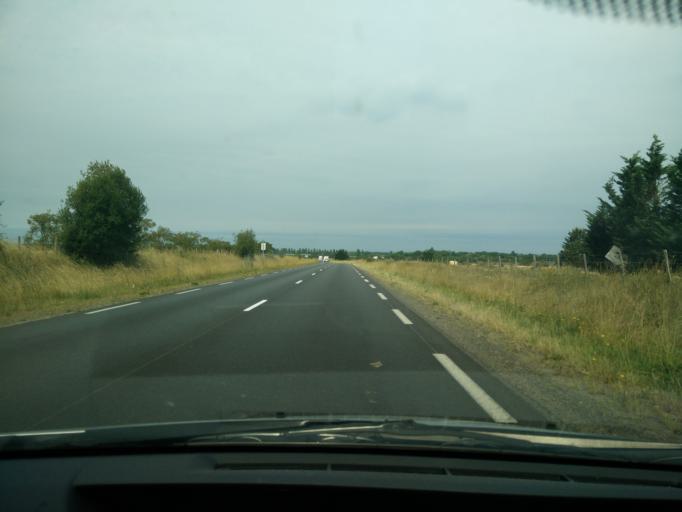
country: FR
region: Pays de la Loire
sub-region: Departement de Maine-et-Loire
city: Doue-la-Fontaine
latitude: 47.1834
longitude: -0.2902
